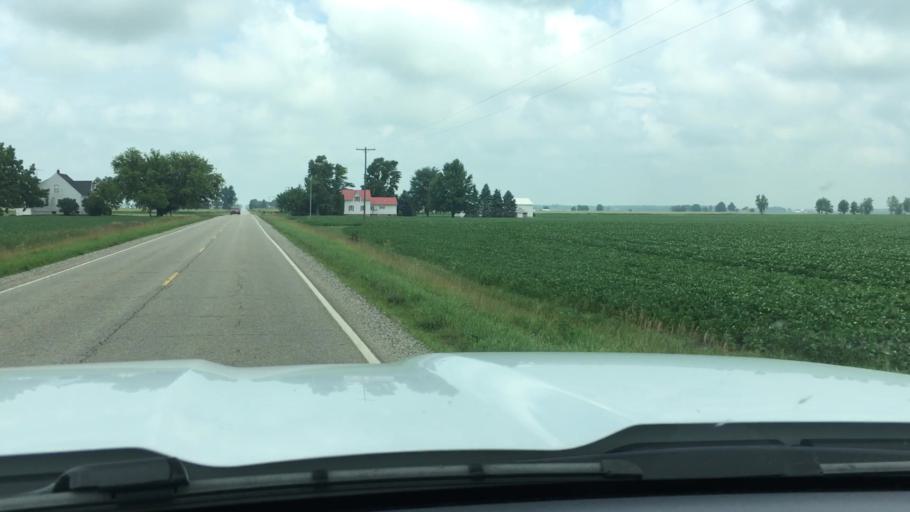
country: US
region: Michigan
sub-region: Sanilac County
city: Marlette
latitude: 43.3740
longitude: -83.0063
